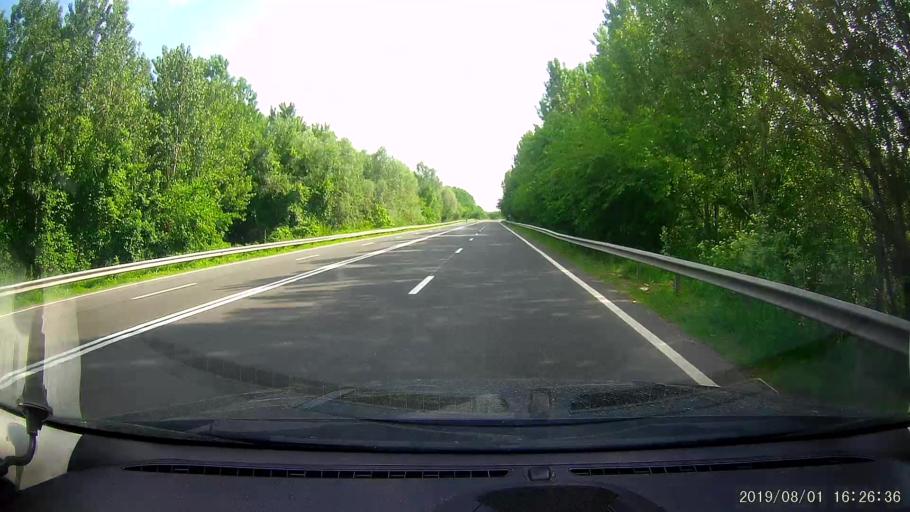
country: RO
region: Calarasi
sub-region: Municipiul Calarasi
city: Calarasi
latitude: 44.1766
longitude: 27.3209
